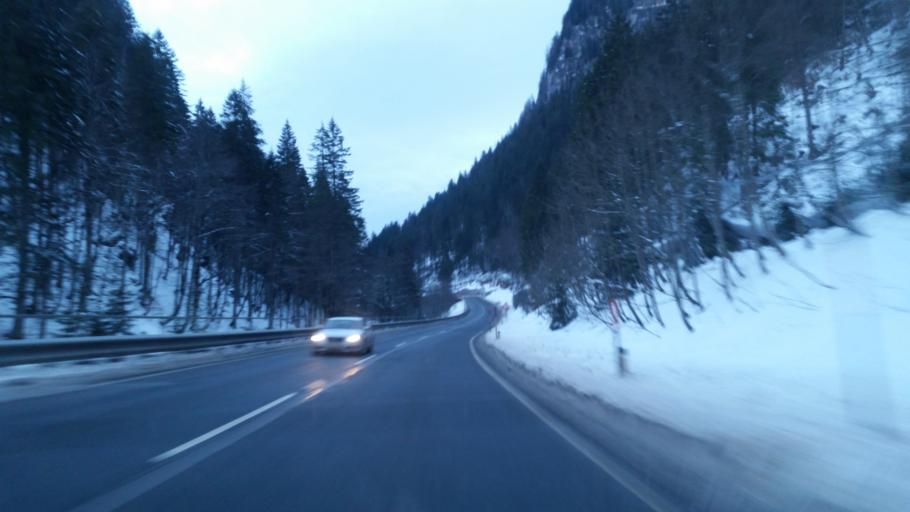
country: AT
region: Salzburg
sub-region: Politischer Bezirk Sankt Johann im Pongau
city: Untertauern
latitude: 47.2824
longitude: 13.5054
